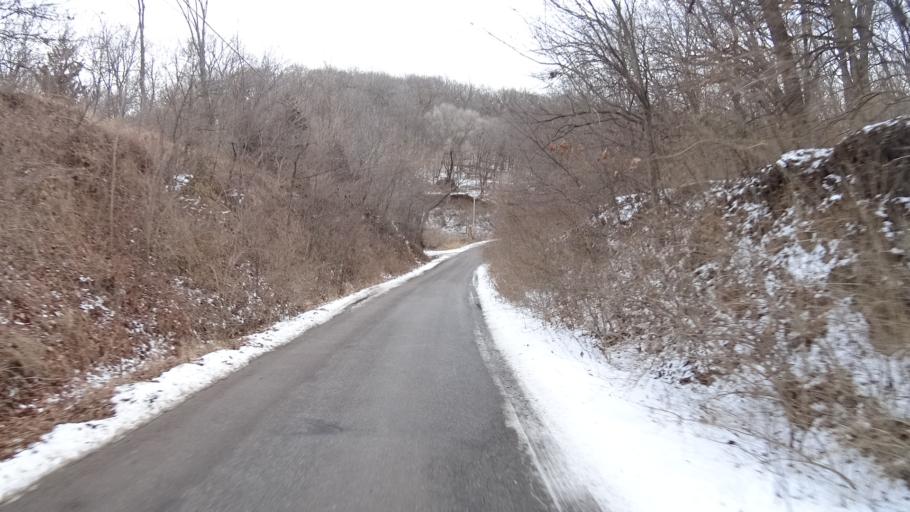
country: US
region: Nebraska
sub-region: Sarpy County
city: Bellevue
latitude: 41.1736
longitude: -95.9080
